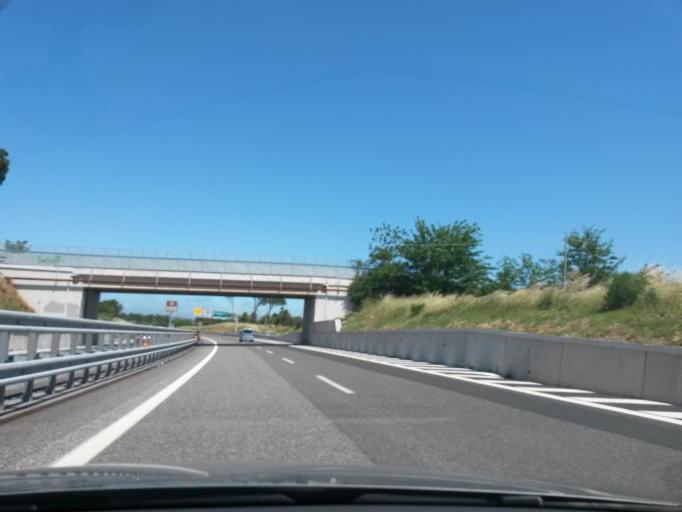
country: IT
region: Tuscany
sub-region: Provincia di Livorno
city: S.P. in Palazzi
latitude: 43.3552
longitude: 10.5137
